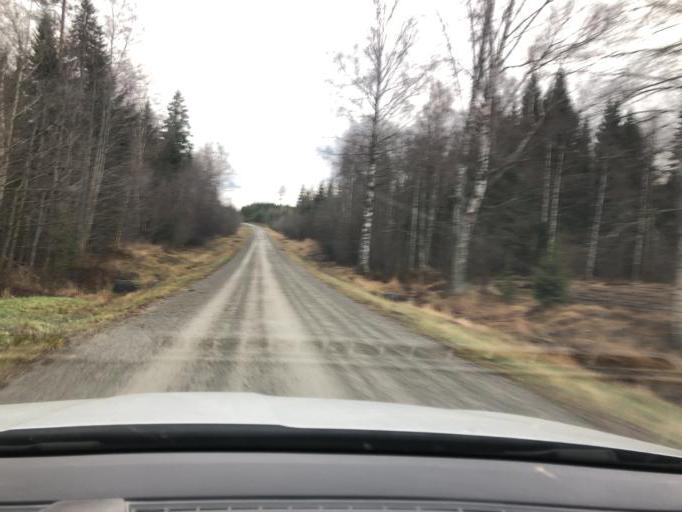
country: SE
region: Gaevleborg
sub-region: Hudiksvalls Kommun
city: Sorforsa
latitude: 61.6525
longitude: 16.9280
